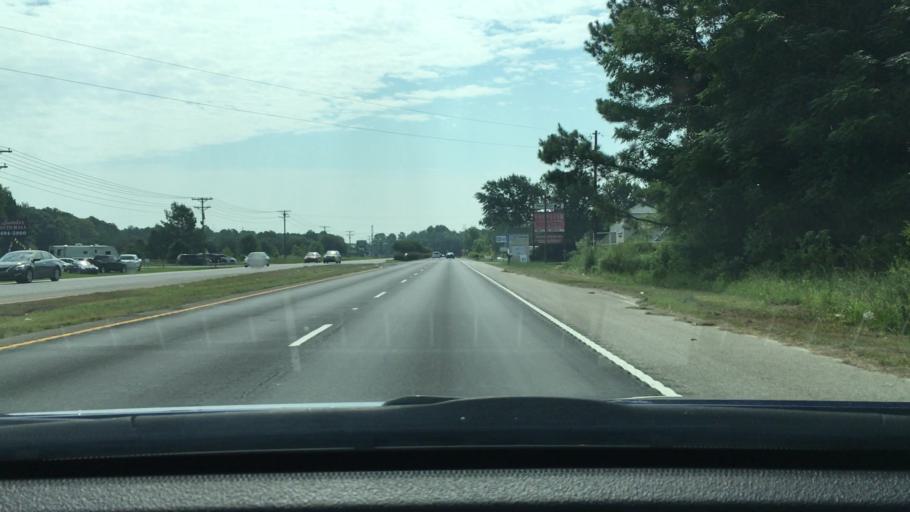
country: US
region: South Carolina
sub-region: Sumter County
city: Cherryvale
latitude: 33.9636
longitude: -80.4346
